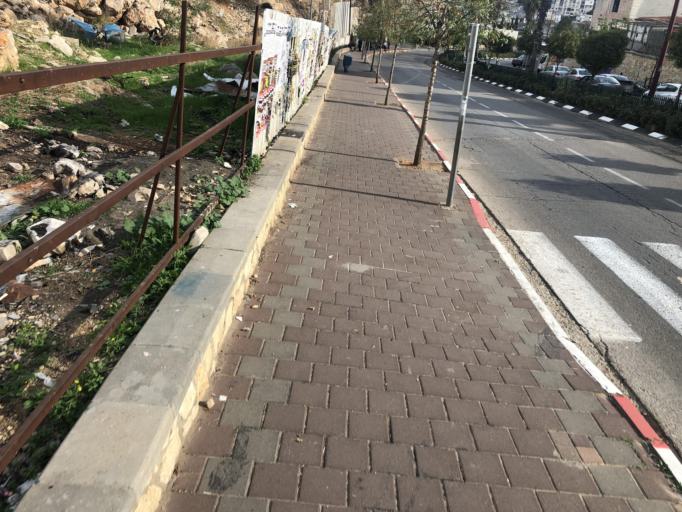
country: IL
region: Jerusalem
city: Modiin Ilit
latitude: 31.9375
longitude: 35.0373
